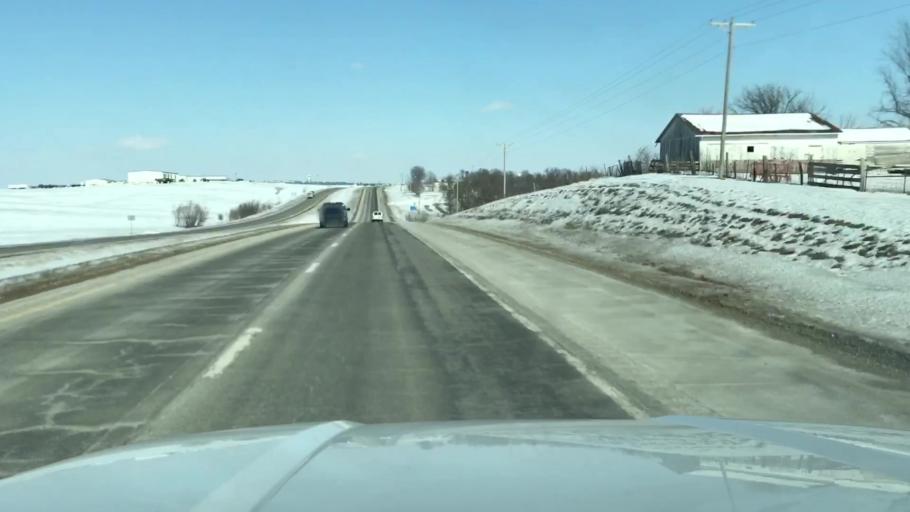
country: US
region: Missouri
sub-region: Nodaway County
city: Maryville
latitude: 40.2929
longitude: -94.8751
